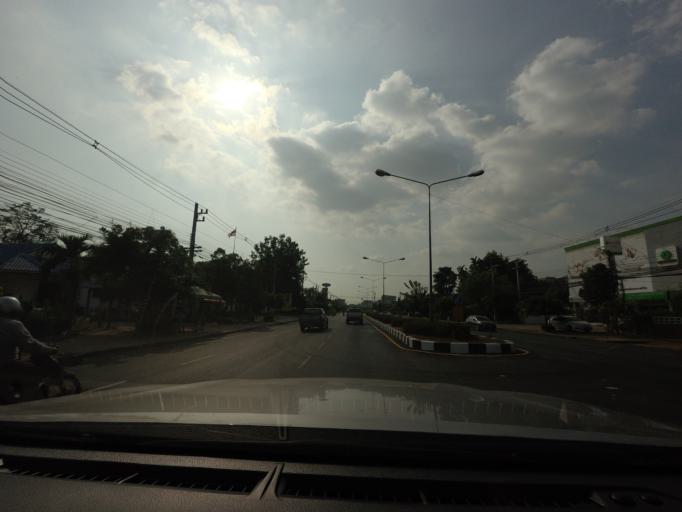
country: TH
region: Sukhothai
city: Sukhothai
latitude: 17.0098
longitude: 99.8319
